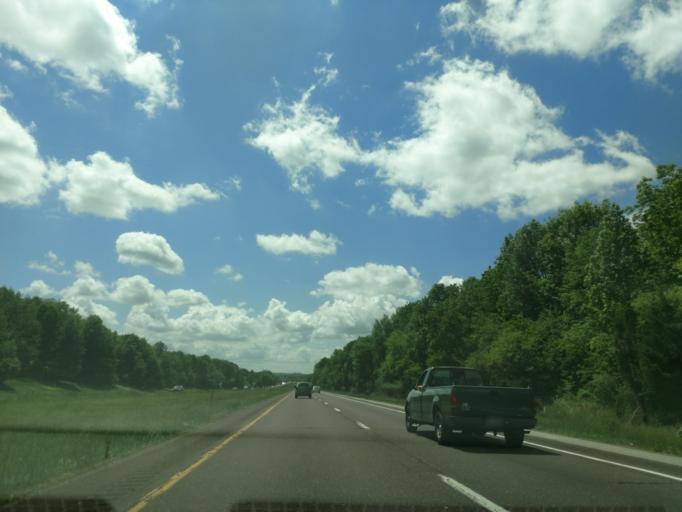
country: US
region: Pennsylvania
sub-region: Montgomery County
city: Audubon
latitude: 40.1158
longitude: -75.4312
